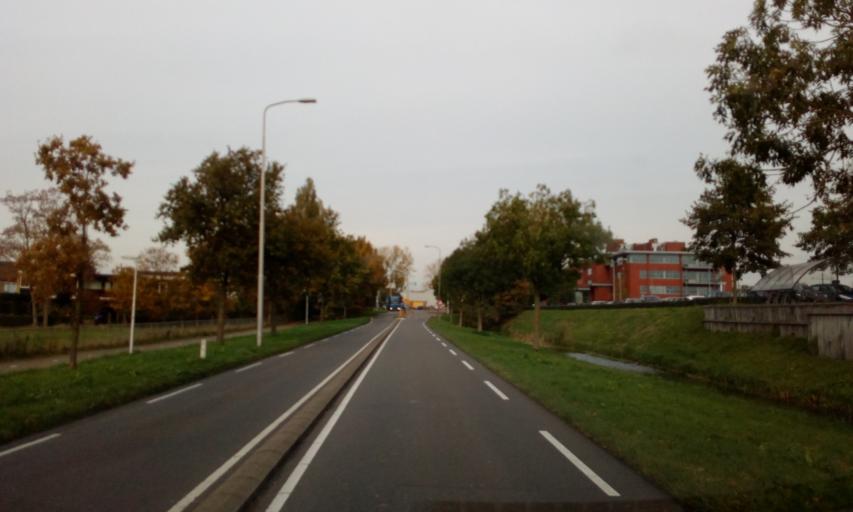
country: NL
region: South Holland
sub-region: Gemeente Lansingerland
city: Berkel en Rodenrijs
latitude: 51.9745
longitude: 4.4596
